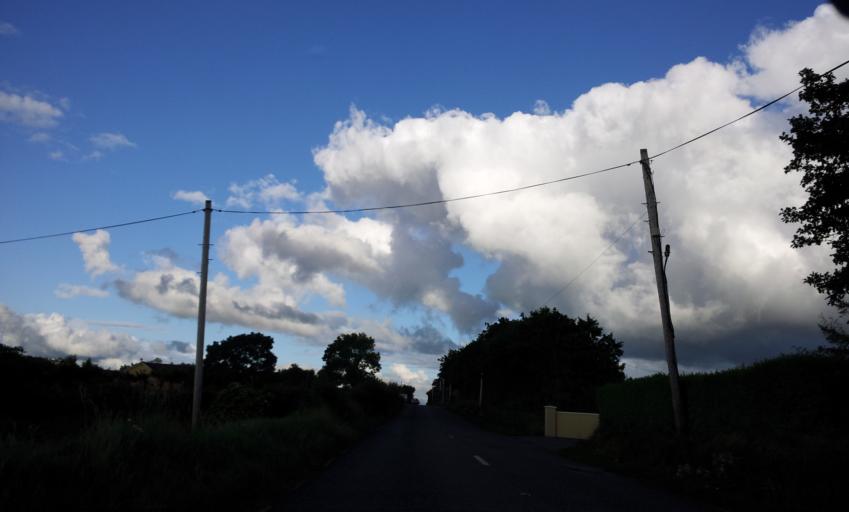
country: IE
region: Munster
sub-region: Ciarrai
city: Tralee
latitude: 52.2428
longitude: -9.7914
